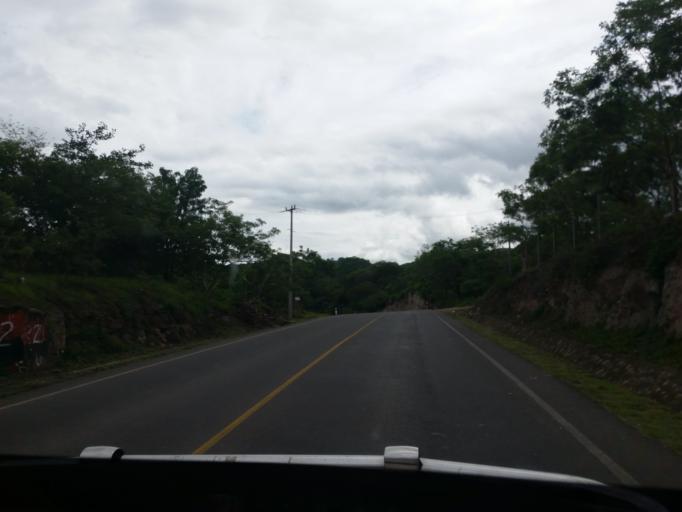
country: NI
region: Matagalpa
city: Ciudad Dario
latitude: 12.8839
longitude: -86.0736
